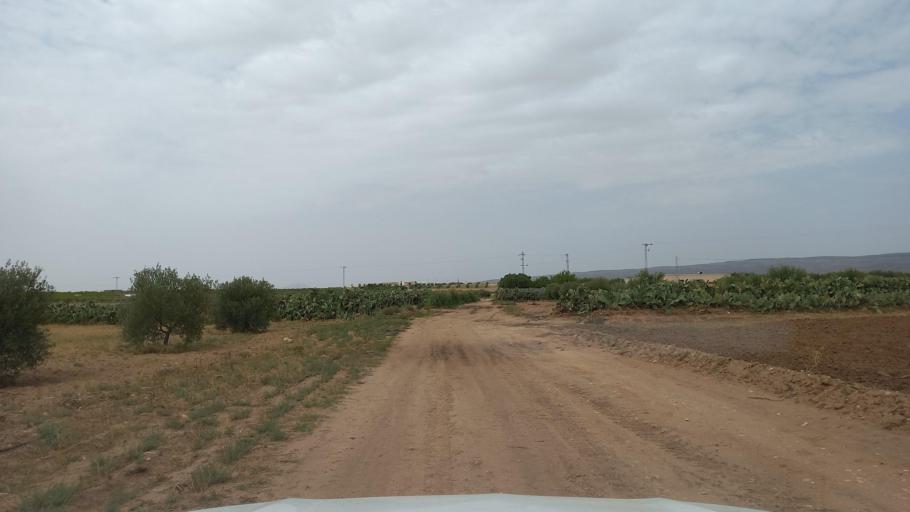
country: TN
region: Al Qasrayn
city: Kasserine
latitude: 35.2867
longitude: 9.0185
